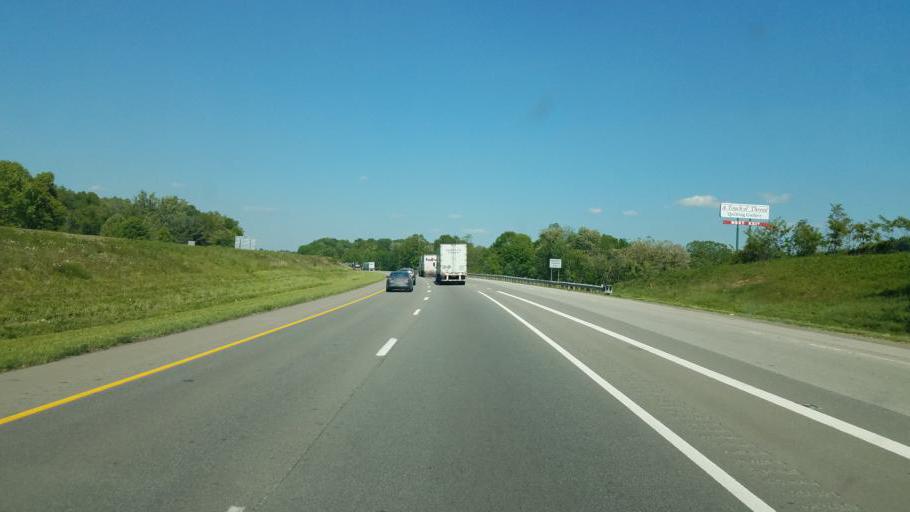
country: US
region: Ohio
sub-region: Muskingum County
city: Pleasant Grove
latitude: 39.9500
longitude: -81.9556
